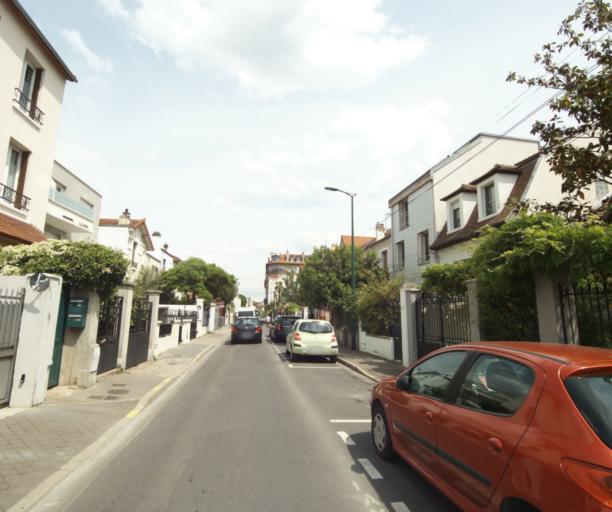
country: FR
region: Ile-de-France
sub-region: Departement des Hauts-de-Seine
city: La Garenne-Colombes
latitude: 48.9124
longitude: 2.2342
